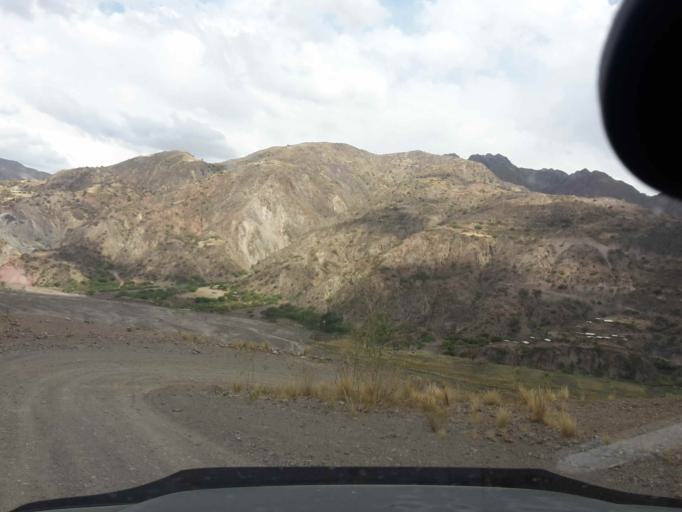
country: BO
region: Cochabamba
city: Colchani
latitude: -17.5164
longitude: -66.6121
